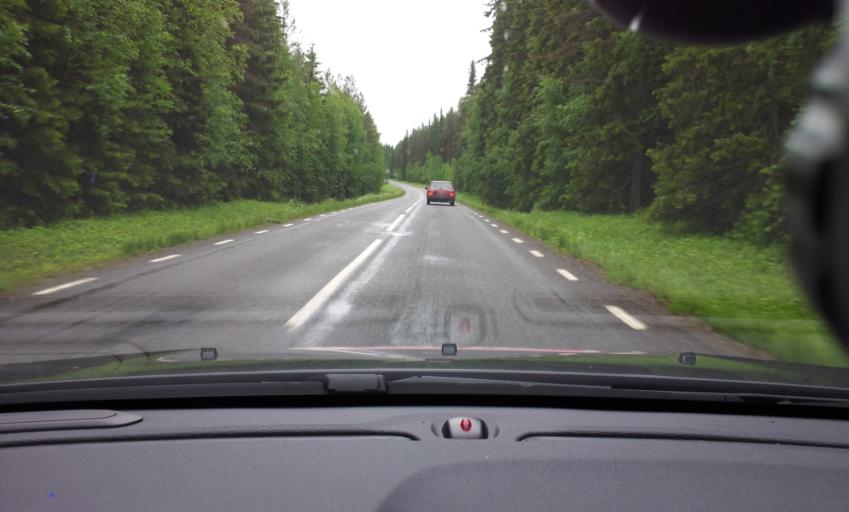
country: SE
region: Jaemtland
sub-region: Stroemsunds Kommun
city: Stroemsund
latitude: 63.4609
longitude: 15.4572
